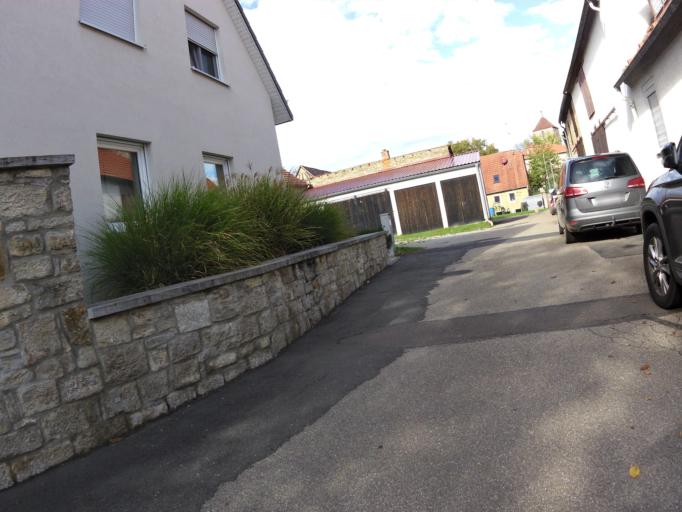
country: DE
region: Bavaria
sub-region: Regierungsbezirk Unterfranken
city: Frickenhausen
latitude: 49.7050
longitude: 10.0801
